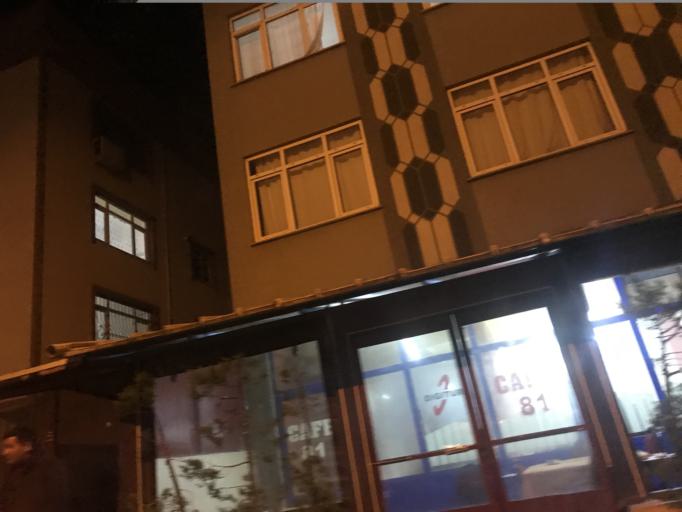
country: TR
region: Istanbul
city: Maltepe
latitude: 40.9232
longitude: 29.1424
